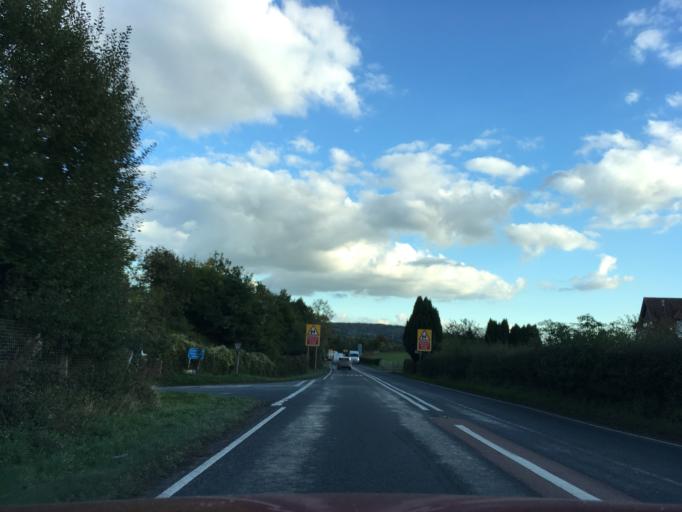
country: GB
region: England
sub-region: Herefordshire
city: Ledbury
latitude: 52.0493
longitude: -2.4472
